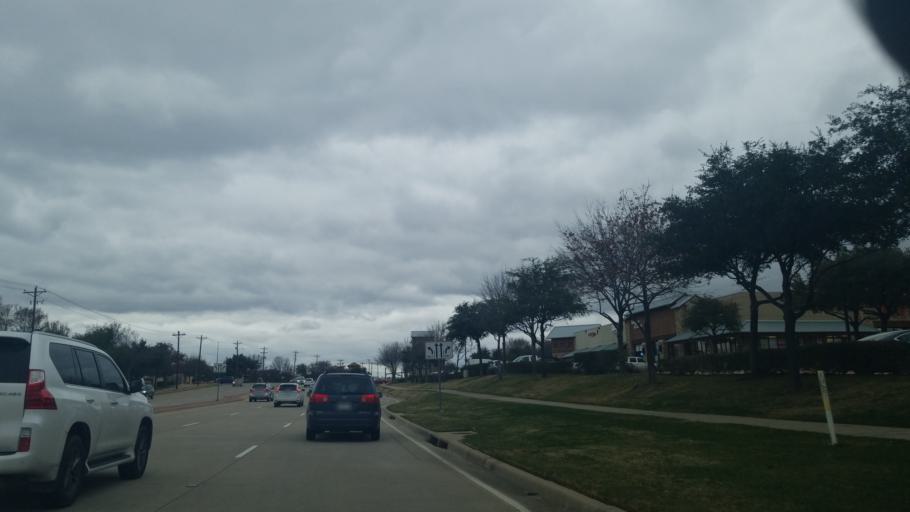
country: US
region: Texas
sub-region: Denton County
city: Double Oak
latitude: 33.0687
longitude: -97.0821
